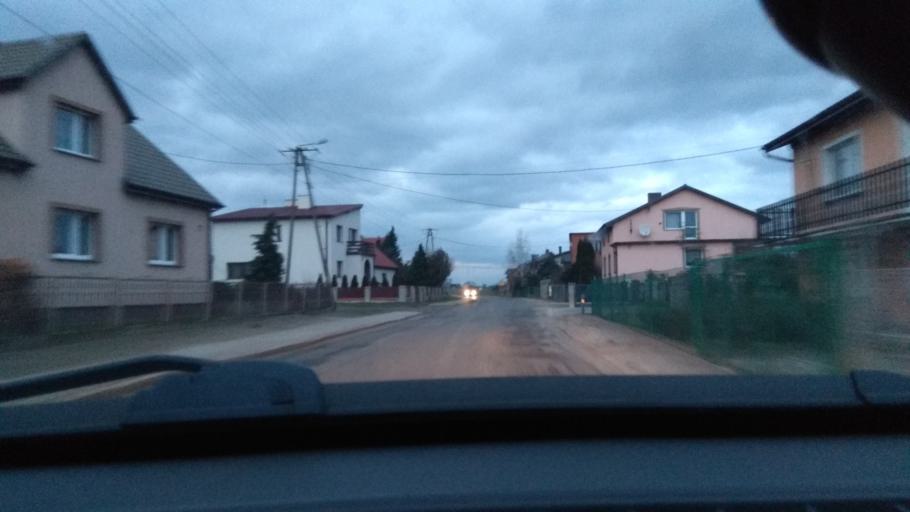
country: PL
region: Lodz Voivodeship
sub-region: Powiat wieruszowski
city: Wieruszow
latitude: 51.3065
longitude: 18.0816
